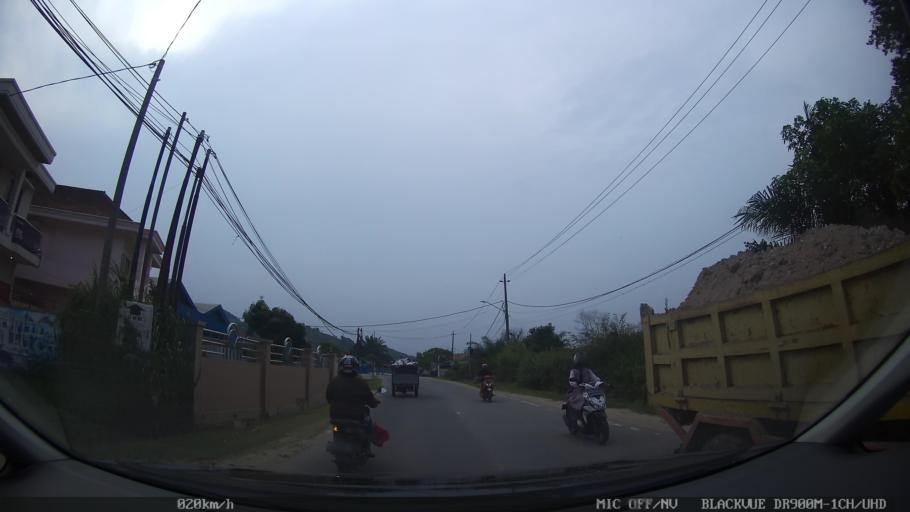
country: ID
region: Lampung
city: Kedaton
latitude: -5.4030
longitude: 105.3168
